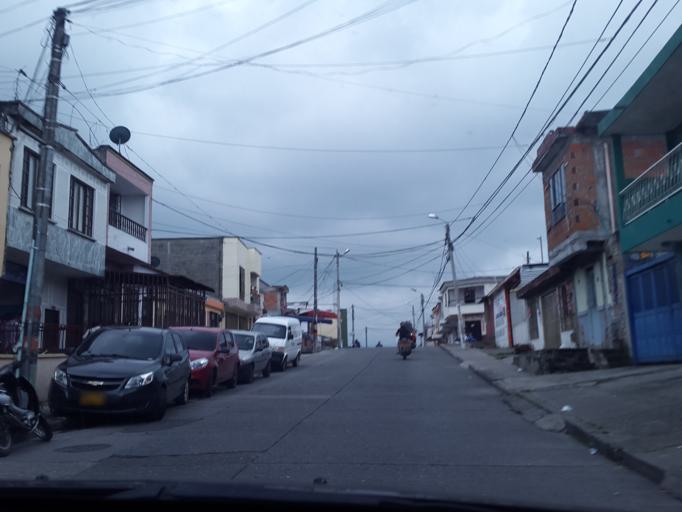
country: CO
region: Quindio
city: Armenia
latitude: 4.5411
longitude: -75.6791
